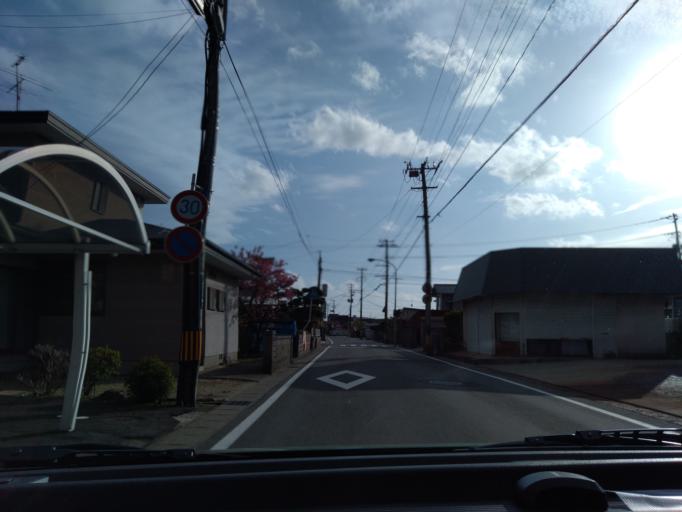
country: JP
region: Akita
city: Akita Shi
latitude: 39.7670
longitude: 140.0788
